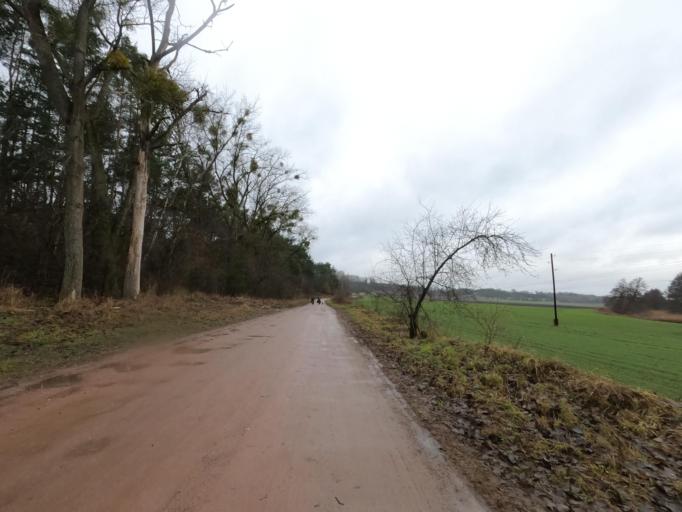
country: PL
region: Greater Poland Voivodeship
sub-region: Powiat pilski
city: Osiek nad Notecia
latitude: 53.1228
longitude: 17.3051
